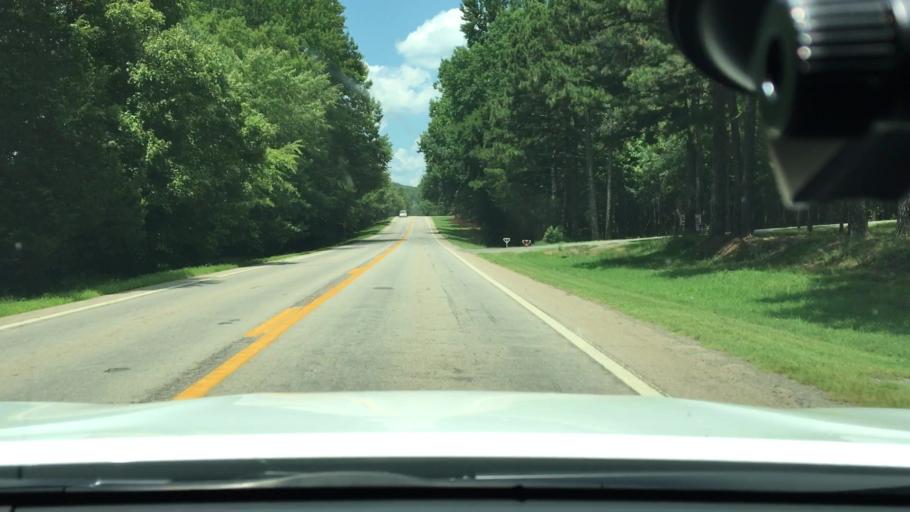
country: US
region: Arkansas
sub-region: Logan County
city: Booneville
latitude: 35.2113
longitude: -93.9301
